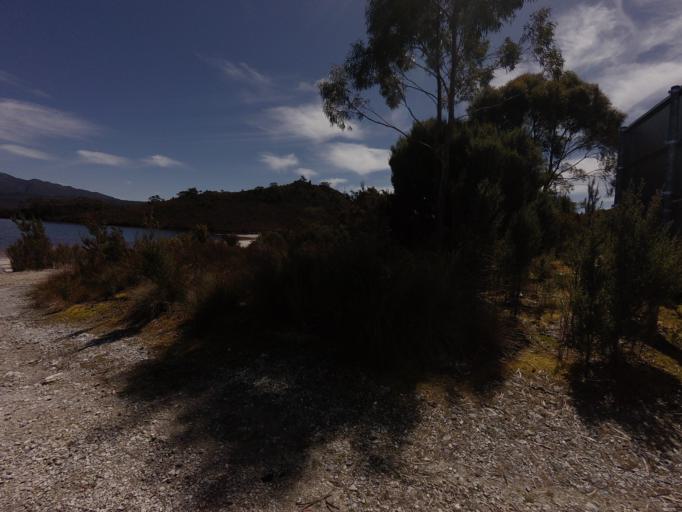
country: AU
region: Tasmania
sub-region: West Coast
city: Queenstown
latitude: -42.7870
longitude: 146.0605
